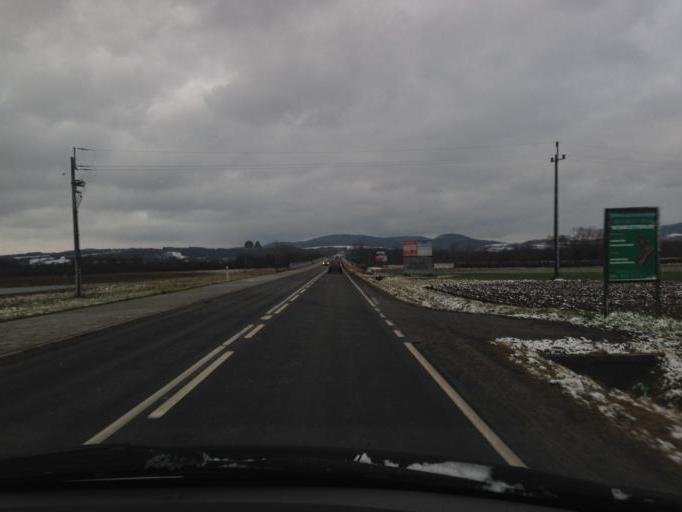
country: PL
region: Lesser Poland Voivodeship
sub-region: Powiat tarnowski
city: Zakliczyn
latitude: 49.8709
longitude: 20.8109
